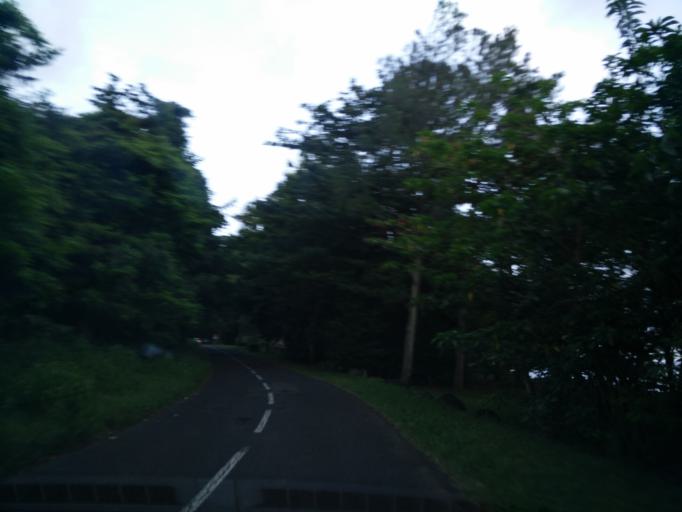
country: MQ
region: Martinique
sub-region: Martinique
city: Saint-Pierre
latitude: 14.8303
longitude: -61.2261
